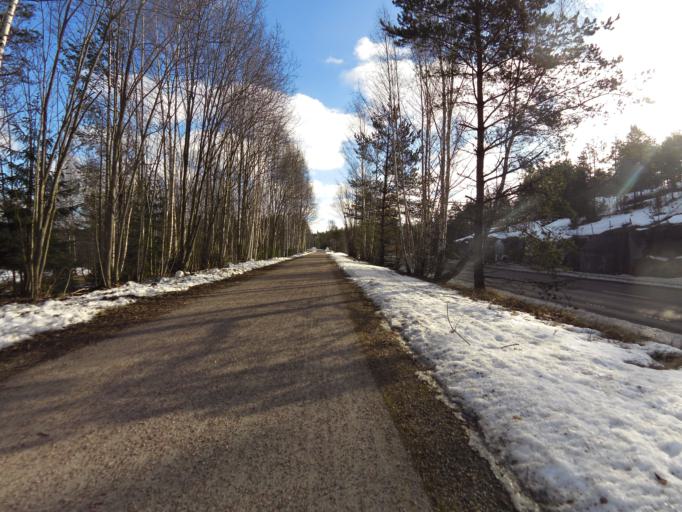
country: SE
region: Gaevleborg
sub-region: Gavle Kommun
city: Gavle
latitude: 60.6498
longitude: 17.1888
